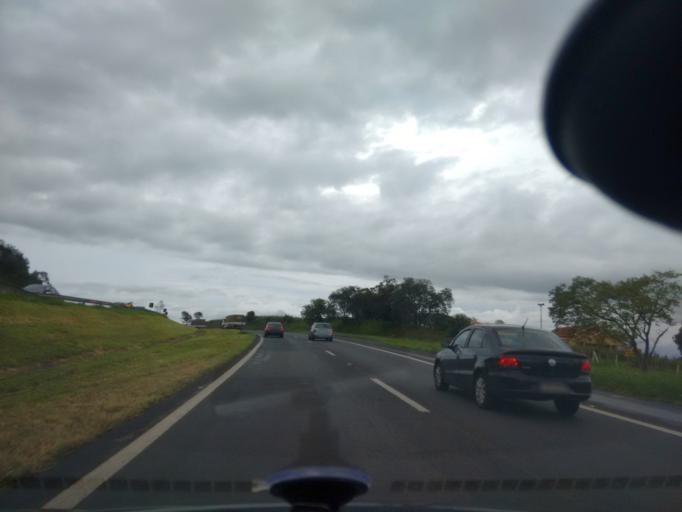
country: BR
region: Sao Paulo
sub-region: Rio Claro
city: Rio Claro
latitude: -22.3244
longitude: -47.6564
